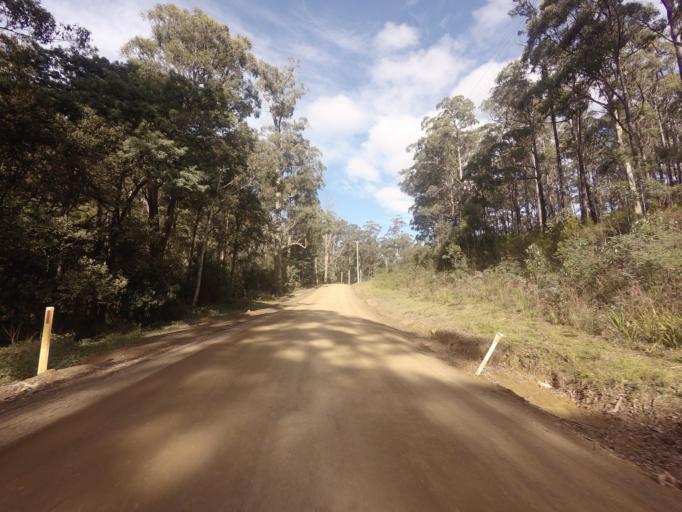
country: AU
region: Tasmania
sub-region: Clarence
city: Sandford
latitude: -43.1251
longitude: 147.7632
